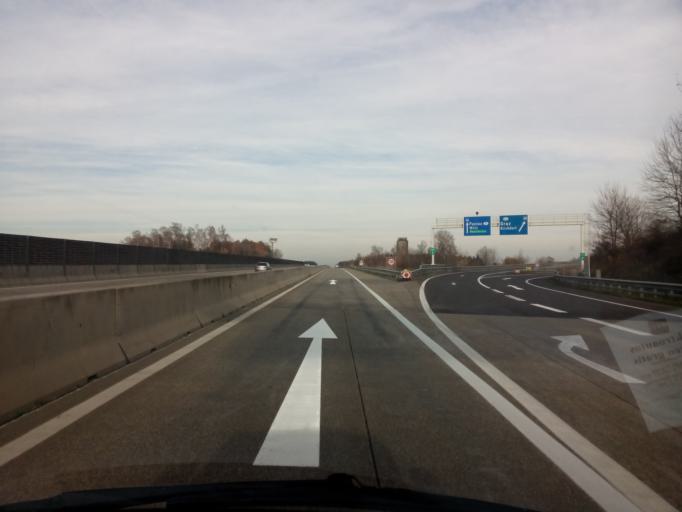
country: AT
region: Upper Austria
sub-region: Wels-Land
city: Sattledt
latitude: 48.0602
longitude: 14.0354
